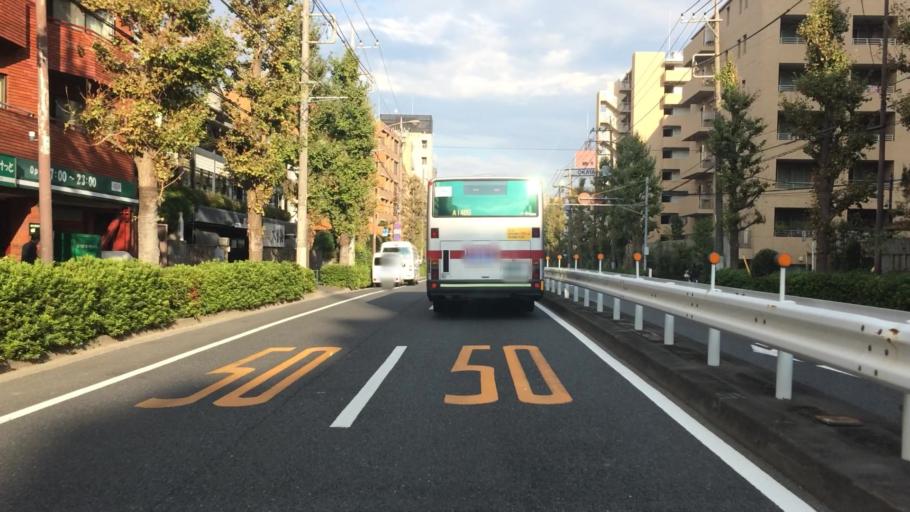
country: JP
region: Tokyo
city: Tokyo
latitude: 35.6129
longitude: 139.6559
